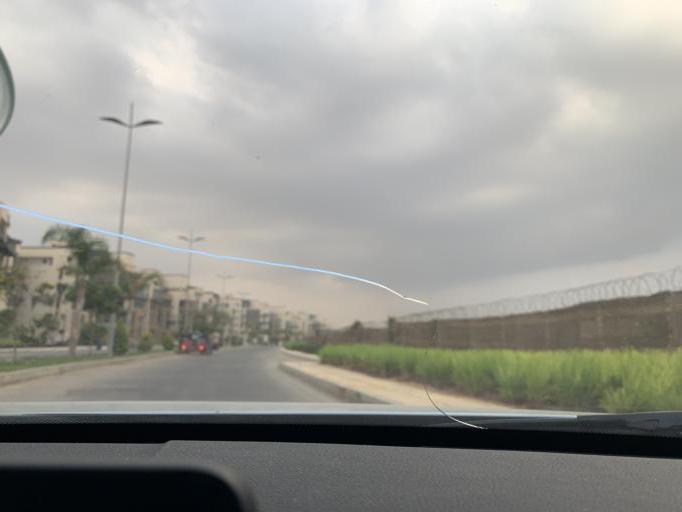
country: EG
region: Muhafazat al Qalyubiyah
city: Al Khankah
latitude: 30.1001
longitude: 31.6587
